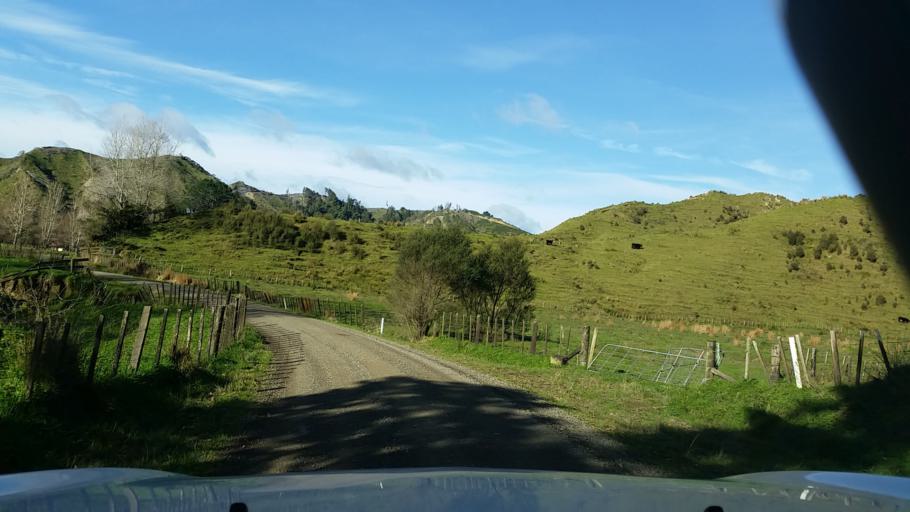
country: NZ
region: Taranaki
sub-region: New Plymouth District
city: Waitara
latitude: -38.9381
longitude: 174.5436
